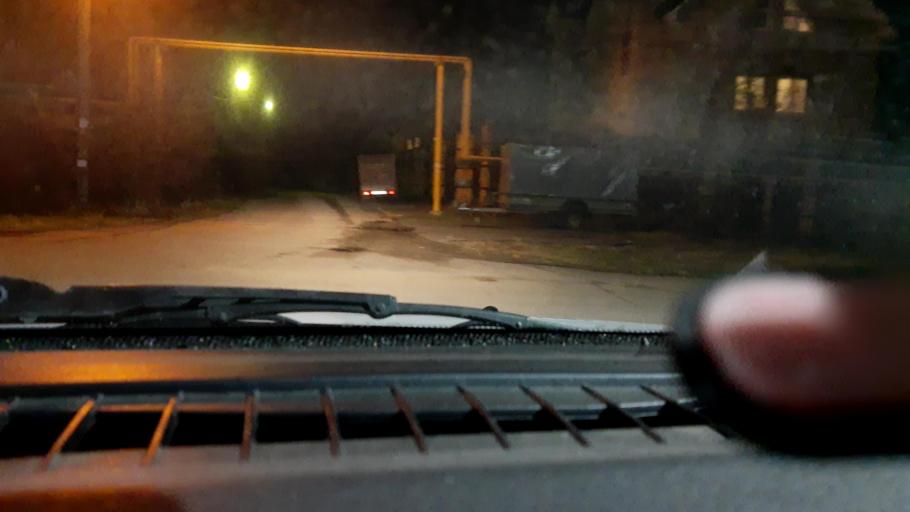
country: RU
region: Nizjnij Novgorod
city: Afonino
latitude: 56.2818
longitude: 44.0625
